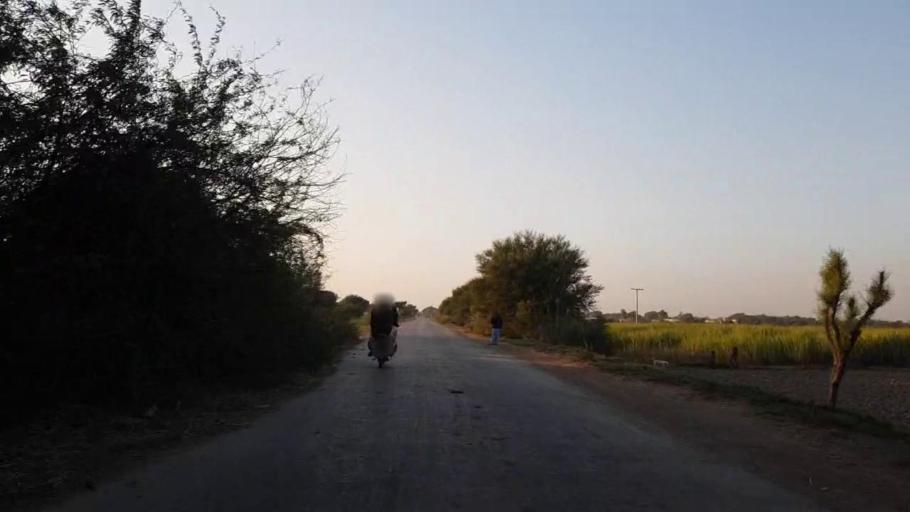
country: PK
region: Sindh
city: Chambar
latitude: 25.2356
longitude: 68.6991
